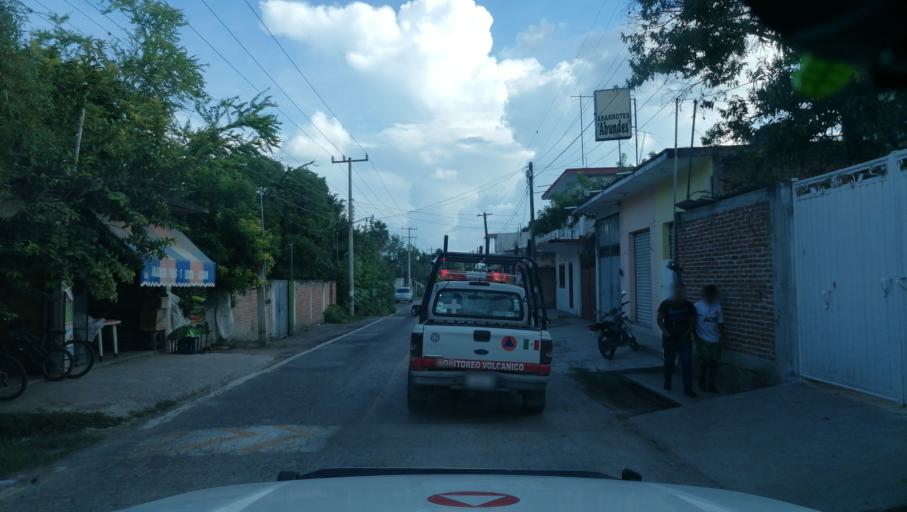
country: MX
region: Morelos
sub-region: Ayala
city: Abelardo L. Rodriguez
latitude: 18.7176
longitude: -98.9908
